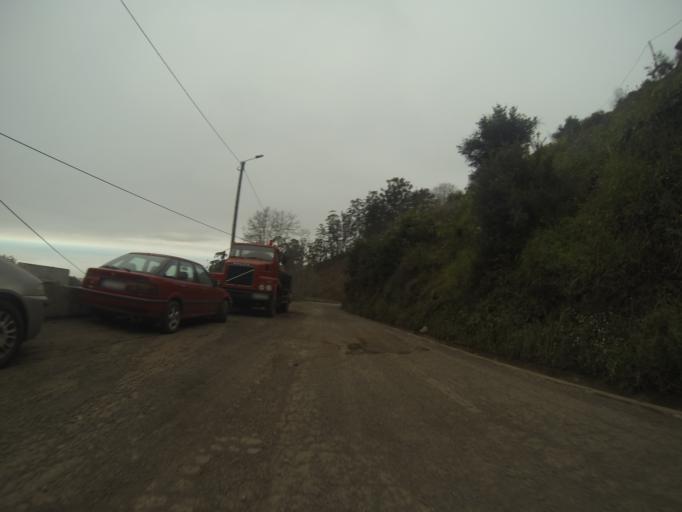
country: PT
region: Madeira
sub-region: Camara de Lobos
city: Curral das Freiras
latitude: 32.6818
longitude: -16.9531
